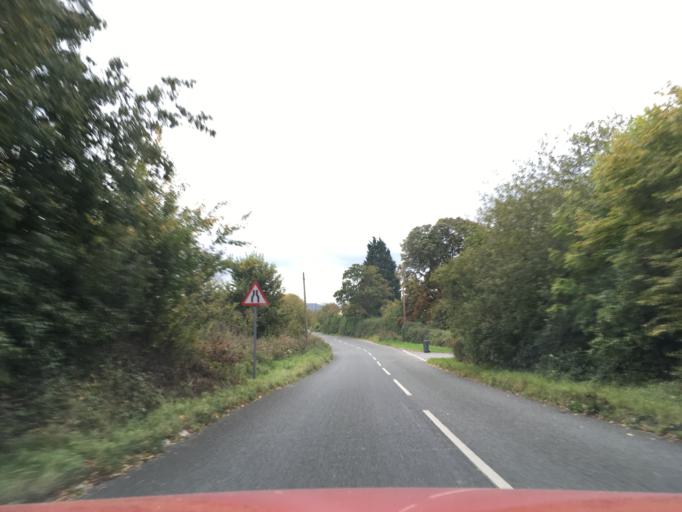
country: GB
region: England
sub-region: Gloucestershire
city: Stonehouse
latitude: 51.7628
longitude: -2.3163
